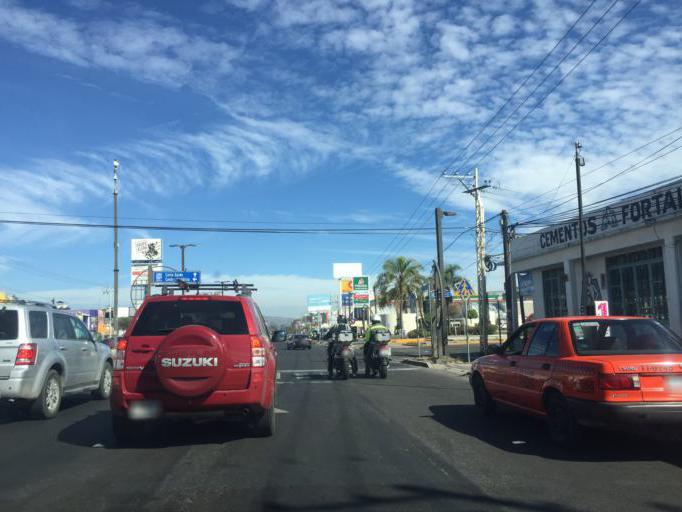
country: MX
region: Queretaro
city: San Juan del Rio
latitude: 20.3876
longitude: -99.9845
